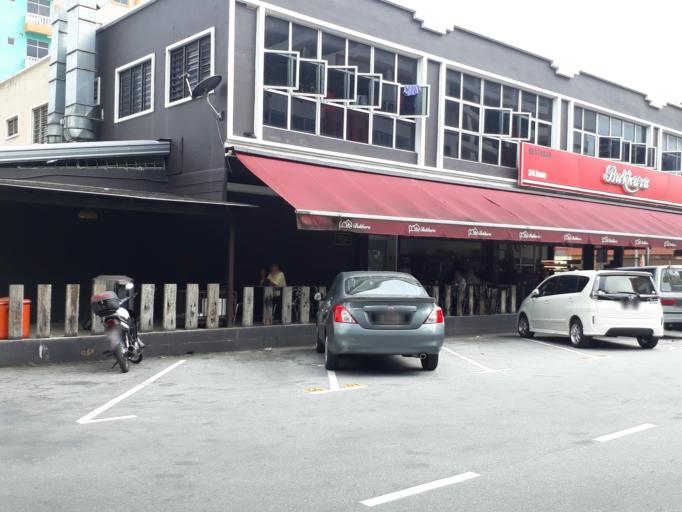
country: MY
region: Perak
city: Ipoh
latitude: 4.5991
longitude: 101.0831
